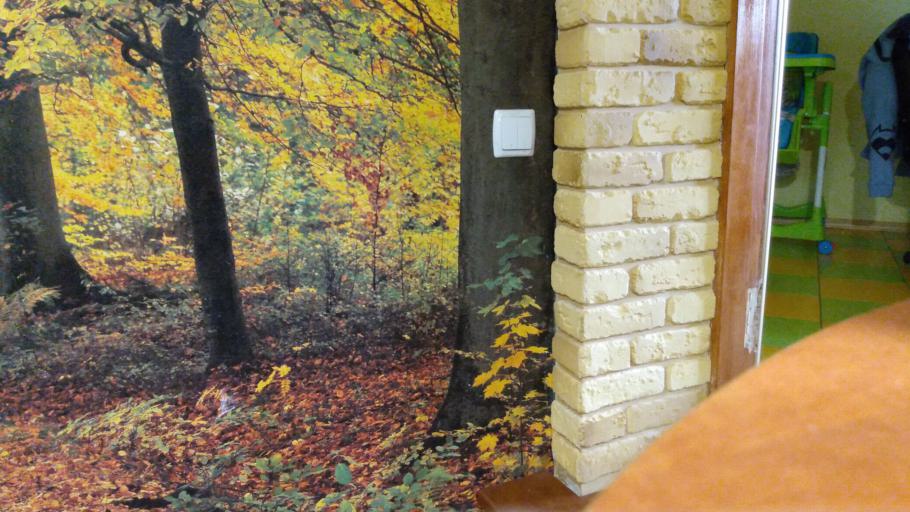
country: RU
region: Pskov
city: Krasnyy Luch
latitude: 57.0835
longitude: 30.2838
